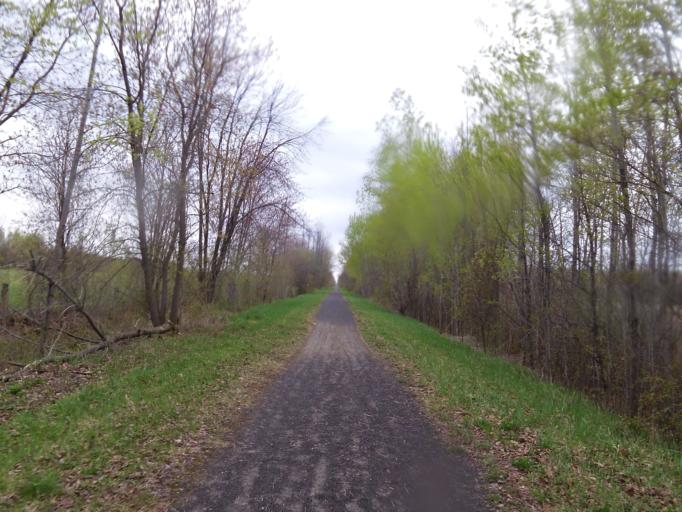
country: CA
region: Ontario
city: Bourget
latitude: 45.4396
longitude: -75.1807
